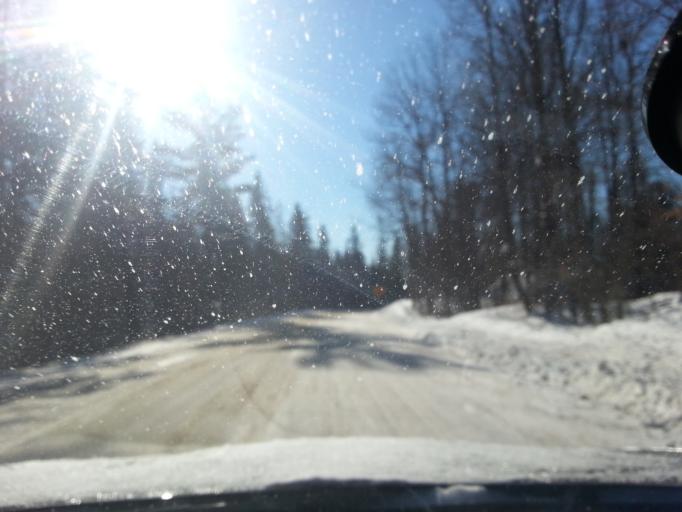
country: CA
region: Ontario
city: Arnprior
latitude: 45.2634
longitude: -76.3250
